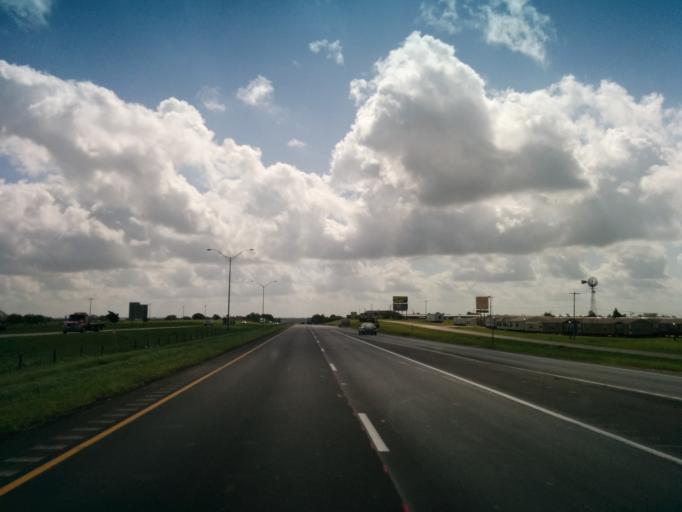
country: US
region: Texas
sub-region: Fayette County
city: Schulenburg
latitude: 29.6940
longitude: -96.8984
